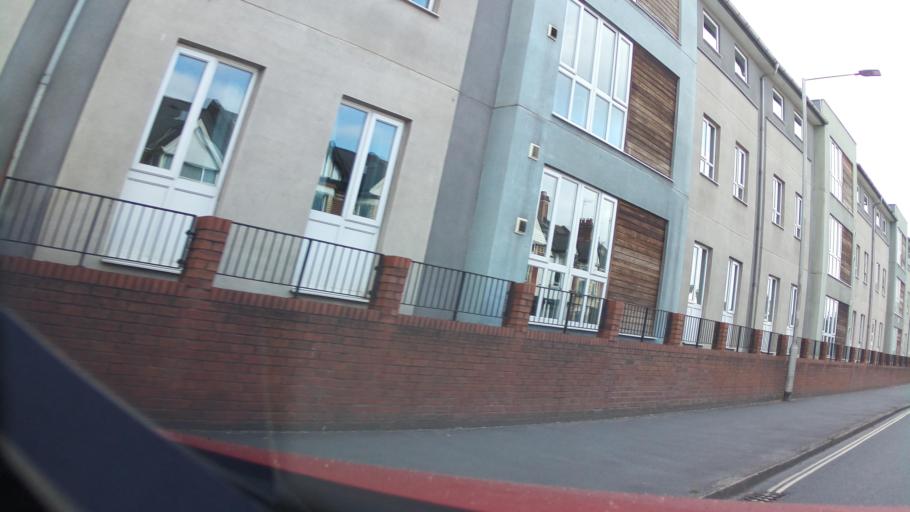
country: GB
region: England
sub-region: Devon
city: Exeter
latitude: 50.7269
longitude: -3.5422
